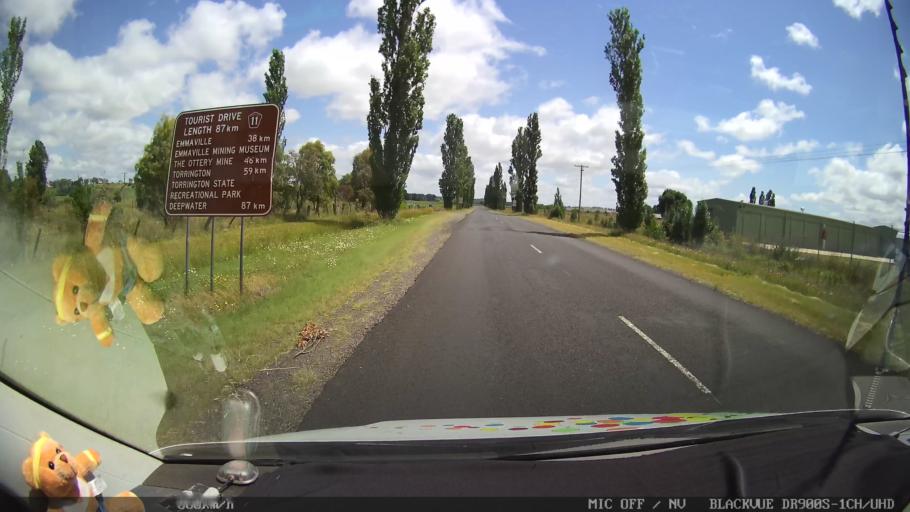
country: AU
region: New South Wales
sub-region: Glen Innes Severn
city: Glen Innes
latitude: -29.7236
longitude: 151.7262
